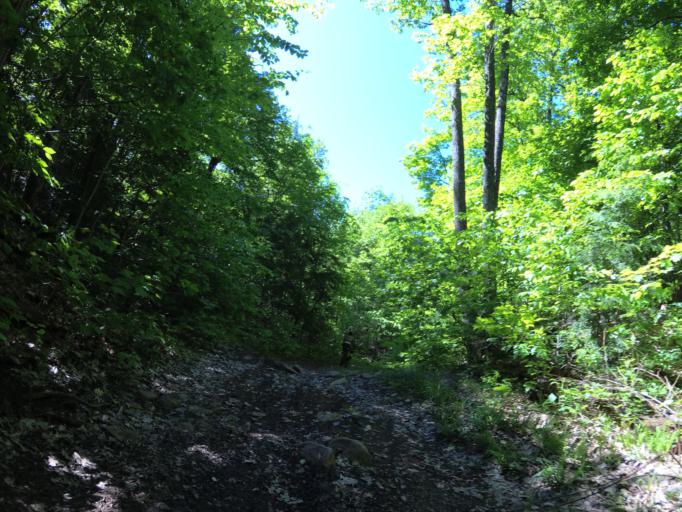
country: CA
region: Ontario
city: Renfrew
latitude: 45.0626
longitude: -77.0803
